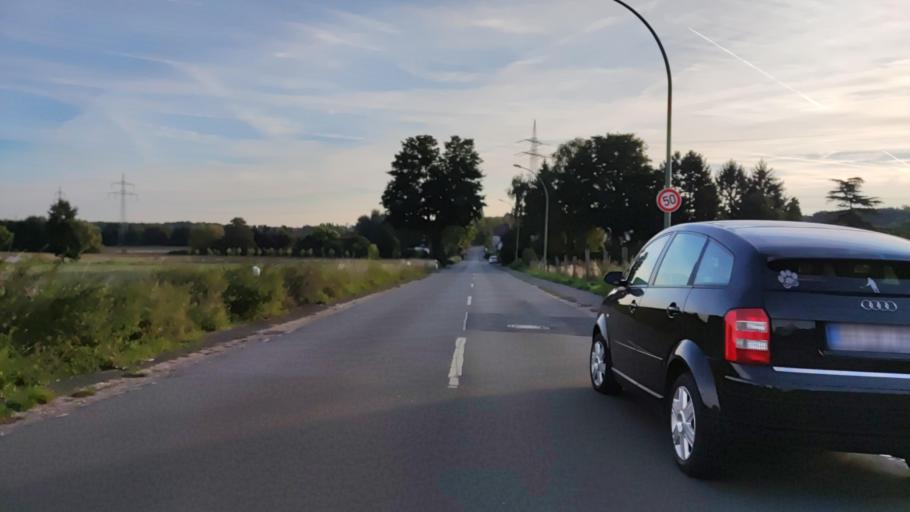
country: DE
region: North Rhine-Westphalia
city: Castrop-Rauxel
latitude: 51.5410
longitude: 7.2905
